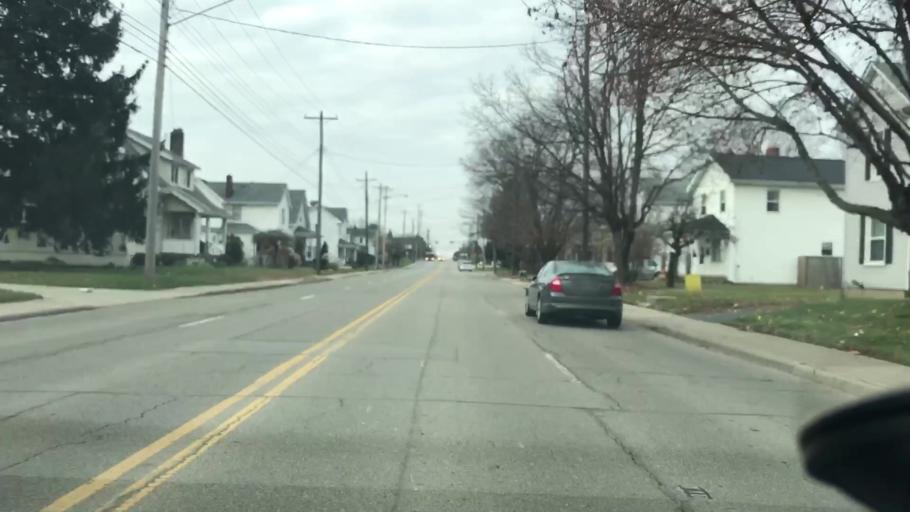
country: US
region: Ohio
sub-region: Franklin County
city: Upper Arlington
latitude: 39.9943
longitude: -83.0877
